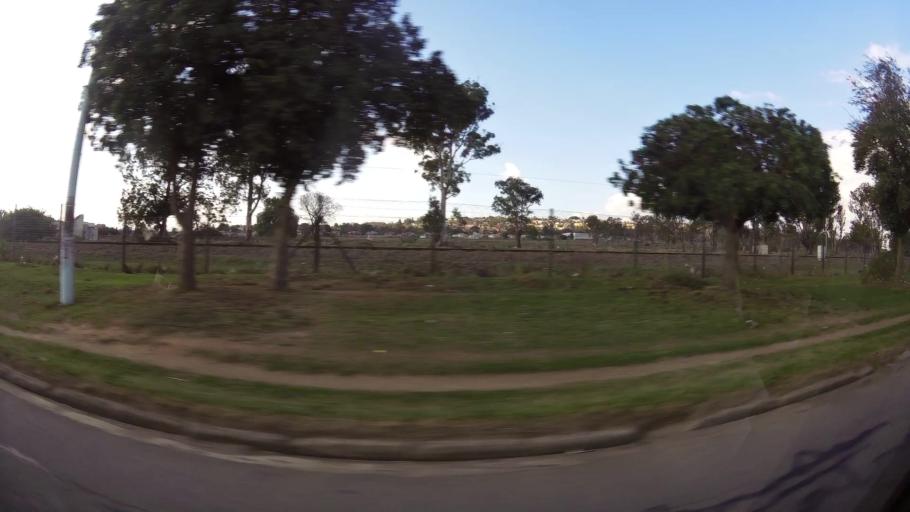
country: ZA
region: Eastern Cape
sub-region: Nelson Mandela Bay Metropolitan Municipality
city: Uitenhage
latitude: -33.7782
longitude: 25.4093
